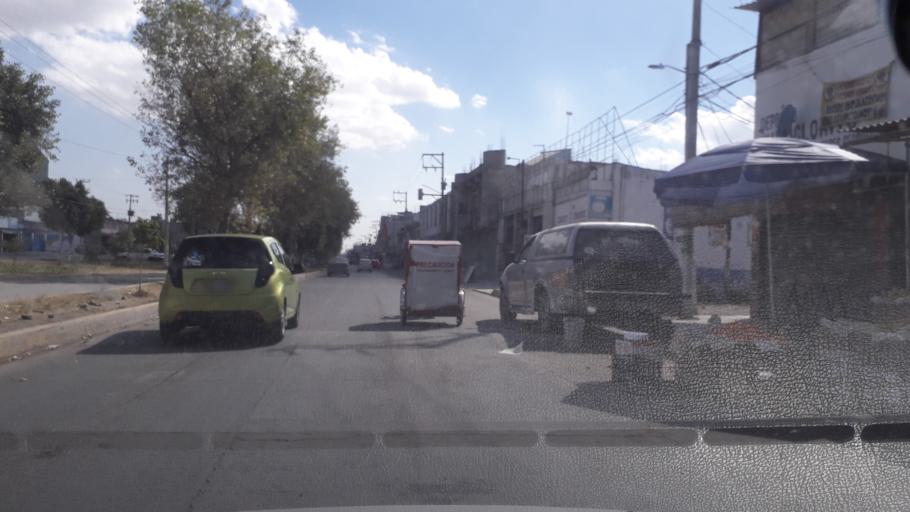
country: MX
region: Mexico
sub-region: Jaltenco
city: Alborada Jaltenco
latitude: 19.6496
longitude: -99.0640
